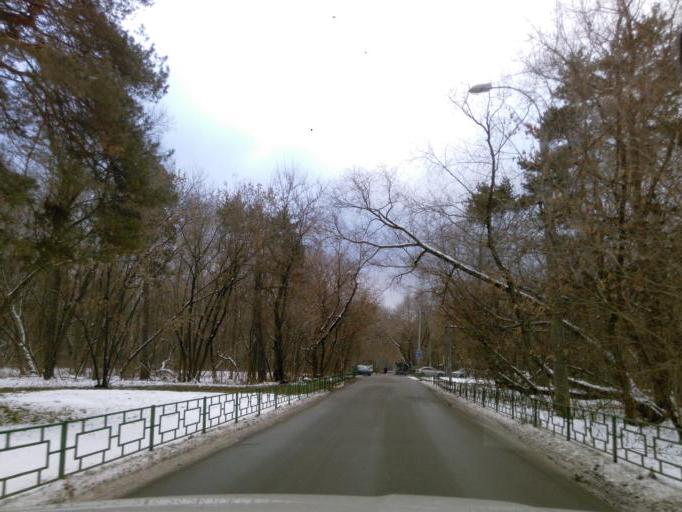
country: RU
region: Moskovskaya
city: Levoberezhnyy
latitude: 55.8278
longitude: 37.4833
